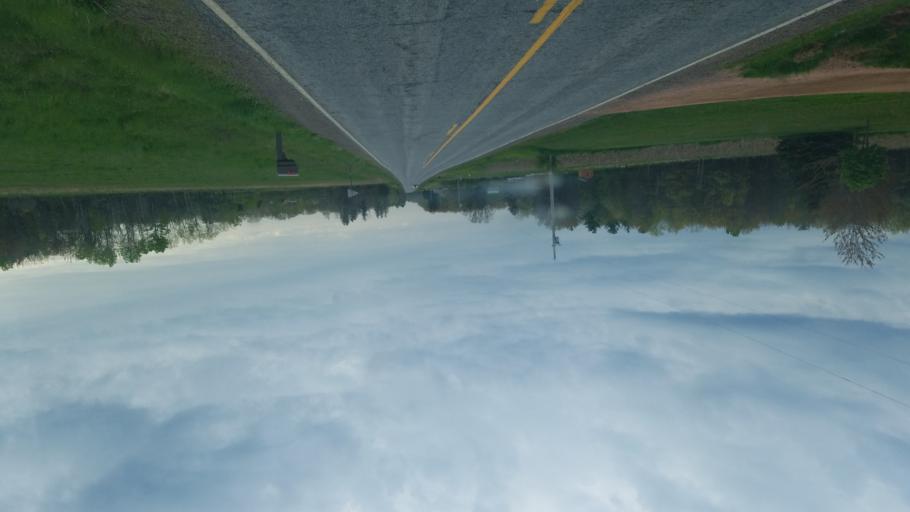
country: US
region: Wisconsin
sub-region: Wood County
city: Nekoosa
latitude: 44.3959
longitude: -90.1602
